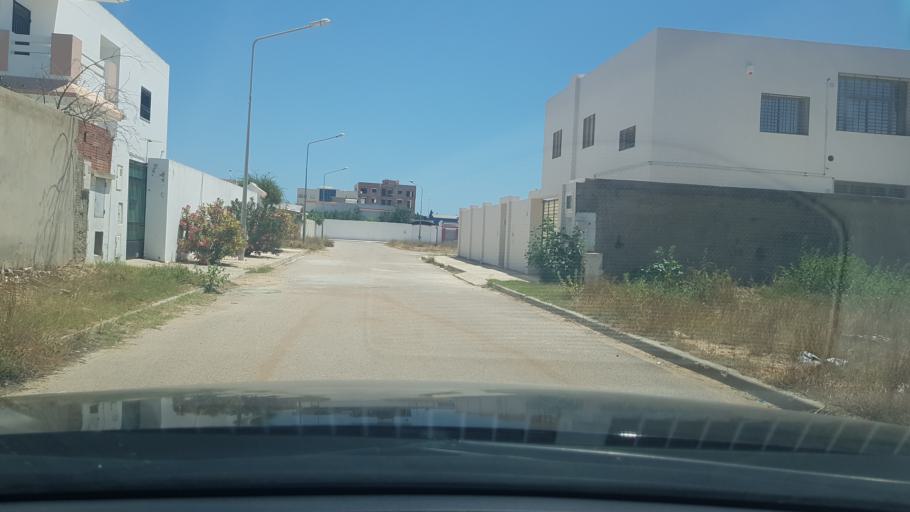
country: TN
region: Safaqis
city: Al Qarmadah
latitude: 34.8375
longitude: 10.7618
